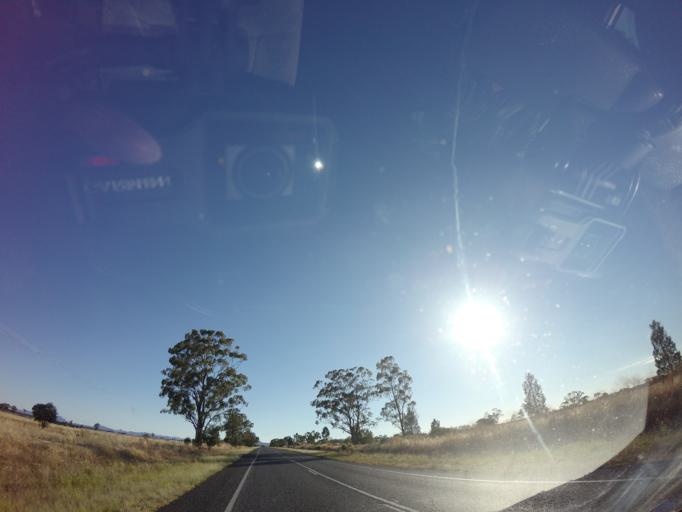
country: AU
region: New South Wales
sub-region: Gilgandra
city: Gilgandra
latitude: -31.5654
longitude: 148.7913
